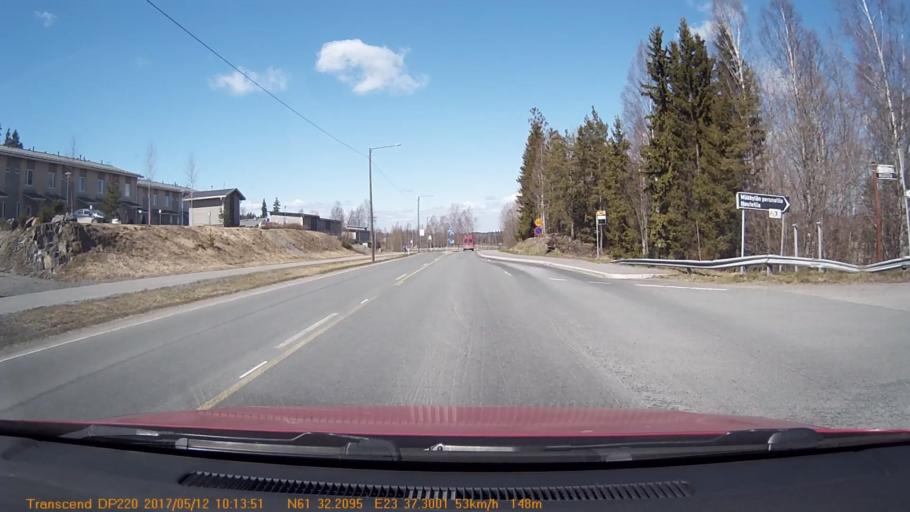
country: FI
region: Pirkanmaa
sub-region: Tampere
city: Yloejaervi
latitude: 61.5366
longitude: 23.6220
